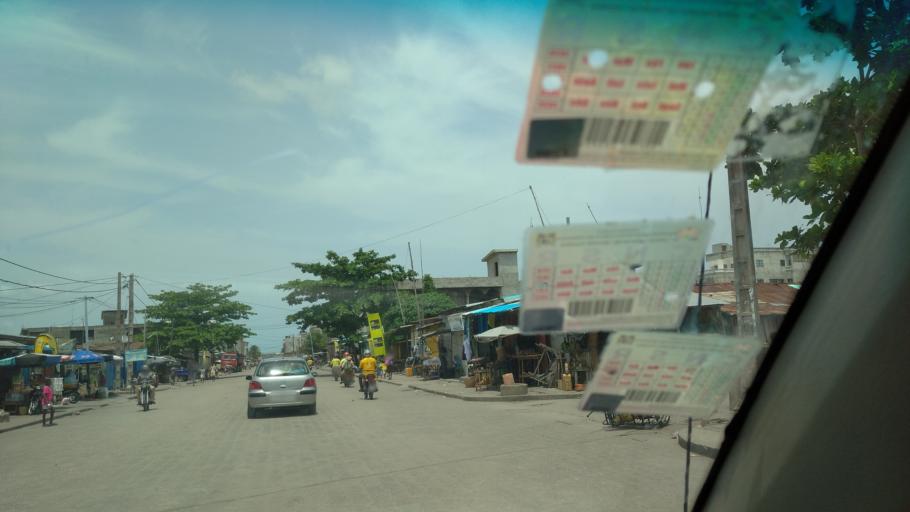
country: BJ
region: Littoral
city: Cotonou
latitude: 6.3904
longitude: 2.4601
